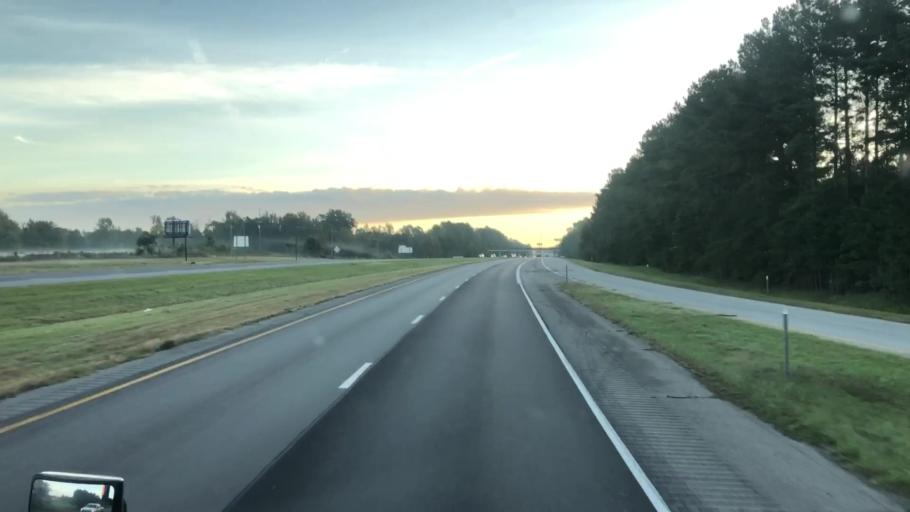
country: US
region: South Carolina
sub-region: Clarendon County
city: Manning
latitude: 33.5903
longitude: -80.3538
